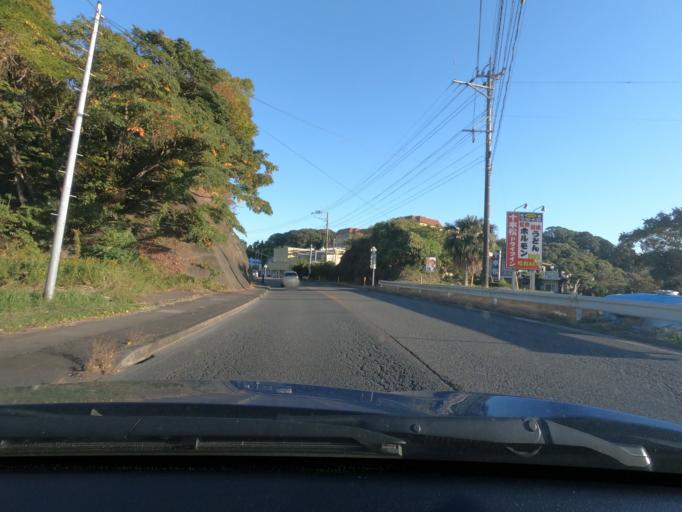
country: JP
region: Kagoshima
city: Satsumasendai
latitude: 31.8606
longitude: 130.2282
